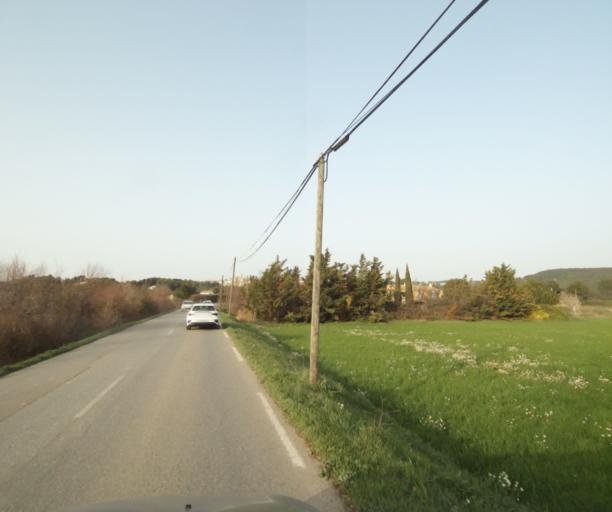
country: FR
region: Provence-Alpes-Cote d'Azur
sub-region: Departement des Bouches-du-Rhone
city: Eguilles
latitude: 43.5576
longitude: 5.3509
